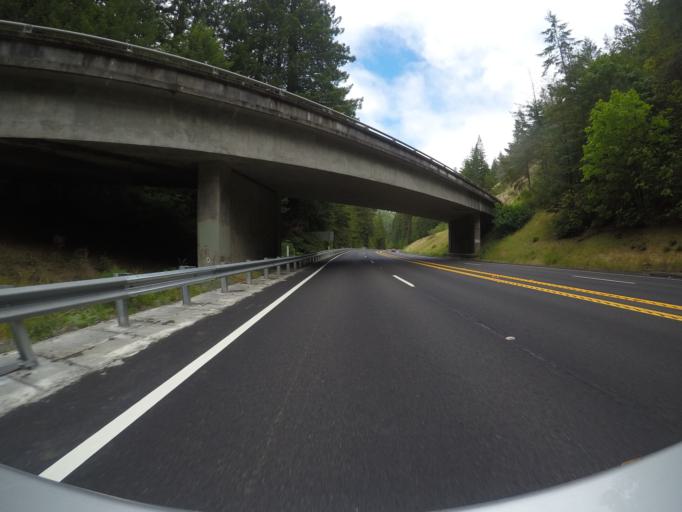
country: US
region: California
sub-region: Humboldt County
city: Rio Dell
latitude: 40.3447
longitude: -123.9316
